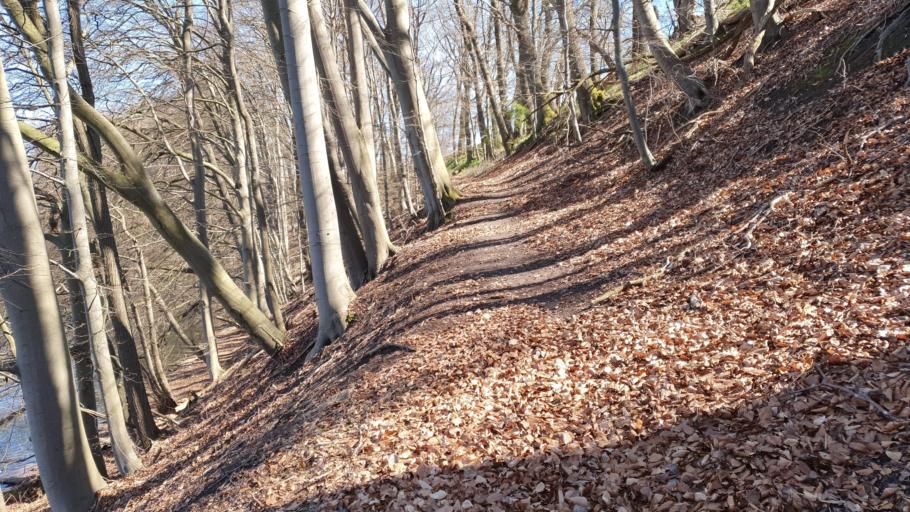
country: DE
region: Mecklenburg-Vorpommern
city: Bruel
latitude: 53.7120
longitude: 11.6975
